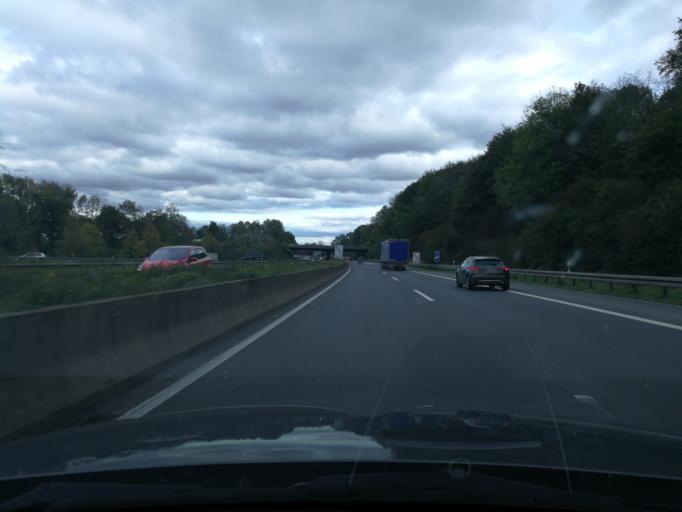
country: DE
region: North Rhine-Westphalia
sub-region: Regierungsbezirk Dusseldorf
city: Monchengladbach
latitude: 51.2234
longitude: 6.4294
